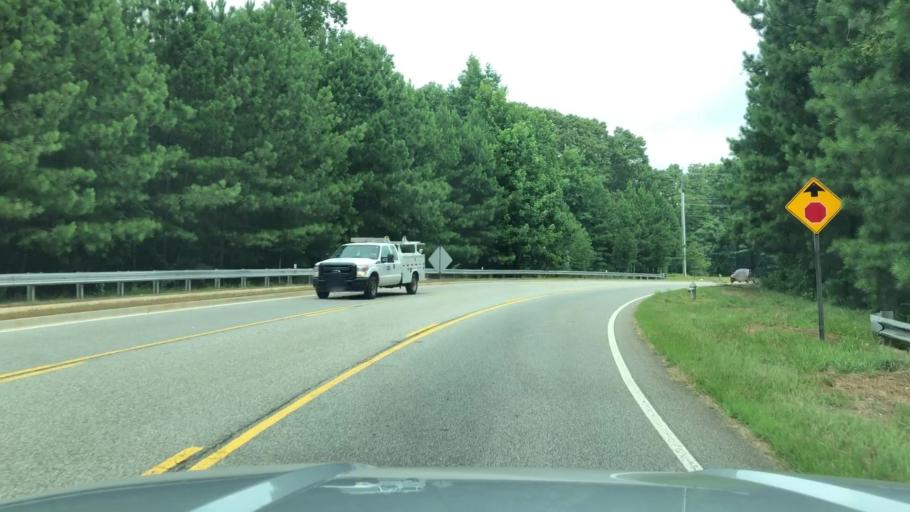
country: US
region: Georgia
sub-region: Cobb County
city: Mableton
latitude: 33.7732
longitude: -84.5806
